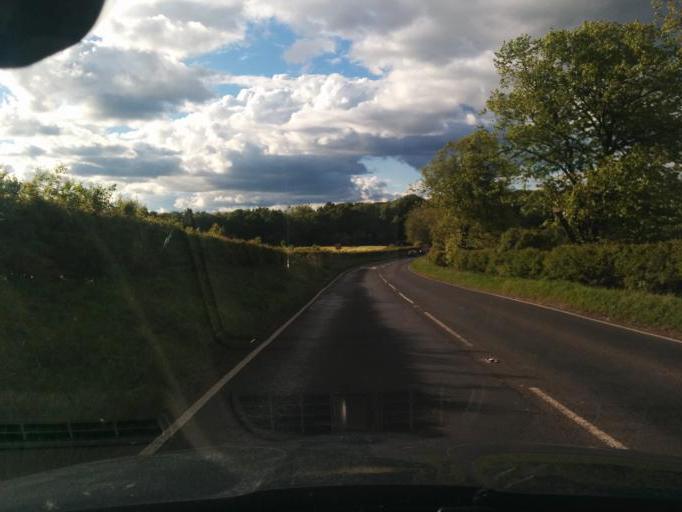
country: GB
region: England
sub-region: Northumberland
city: Bedlington
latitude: 55.1104
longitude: -1.6192
